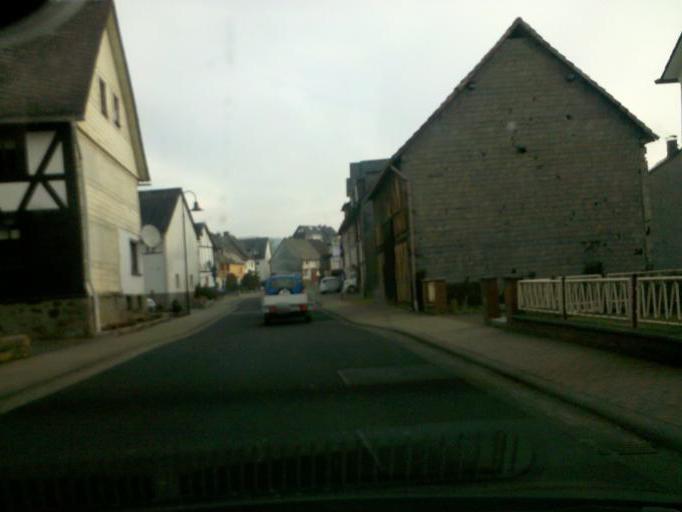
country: DE
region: Hesse
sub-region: Regierungsbezirk Giessen
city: Haiger
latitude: 50.7890
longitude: 8.2266
